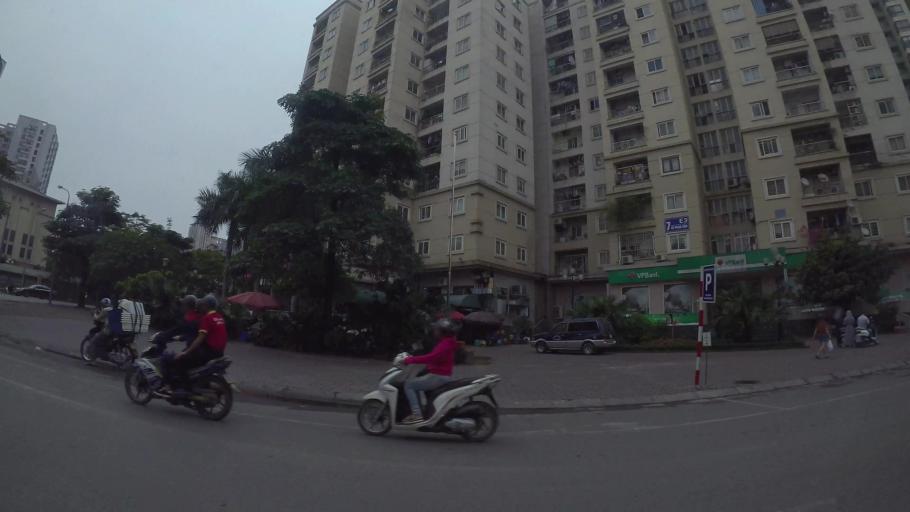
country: VN
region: Ha Noi
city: Cau Giay
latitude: 21.0177
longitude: 105.7987
